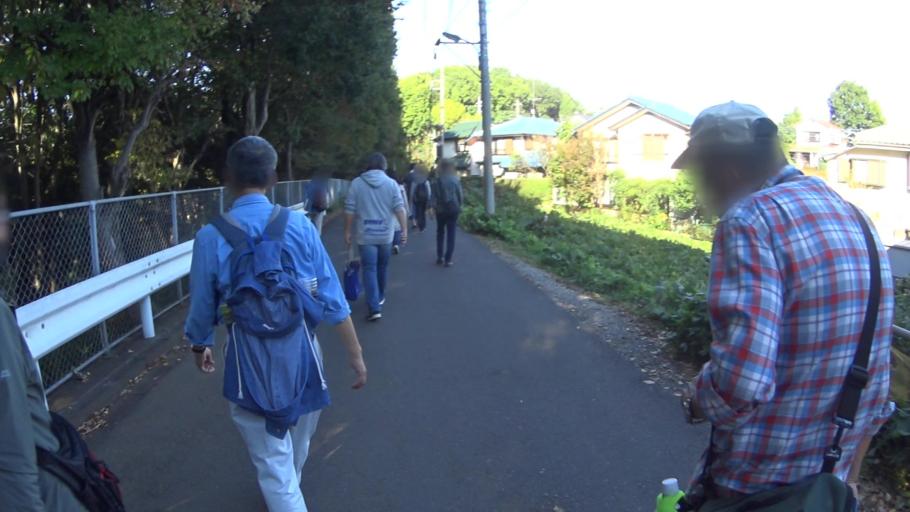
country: JP
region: Tokyo
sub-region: Machida-shi
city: Machida
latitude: 35.5768
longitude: 139.4387
